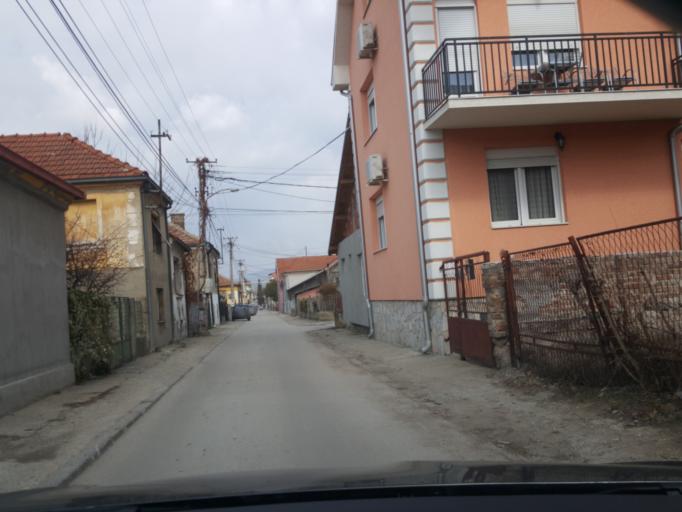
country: RS
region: Central Serbia
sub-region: Nisavski Okrug
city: Nis
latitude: 43.3124
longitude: 21.8716
